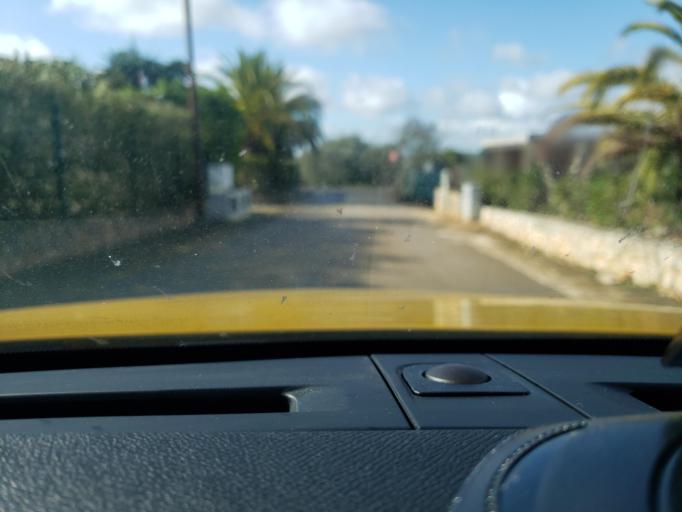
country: PT
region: Faro
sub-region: Portimao
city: Alvor
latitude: 37.1858
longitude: -8.5859
